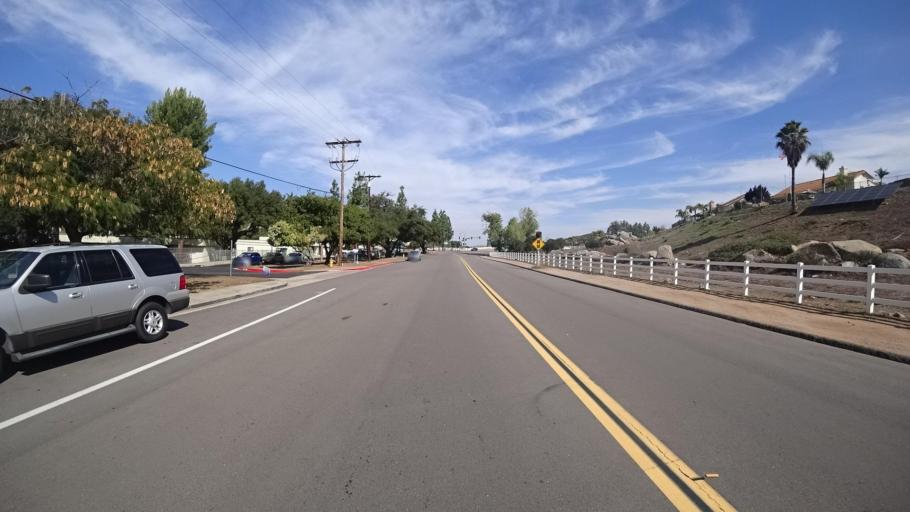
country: US
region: California
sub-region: San Diego County
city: Harbison Canyon
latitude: 32.8324
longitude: -116.8151
